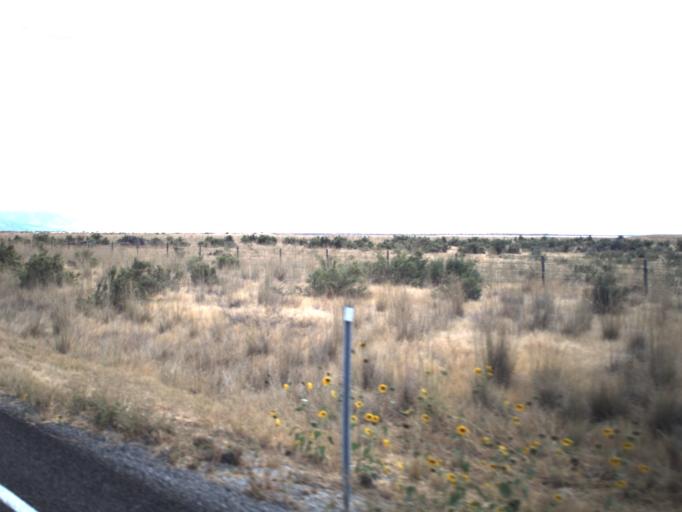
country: US
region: Utah
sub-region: Box Elder County
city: Tremonton
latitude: 41.5896
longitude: -112.2724
